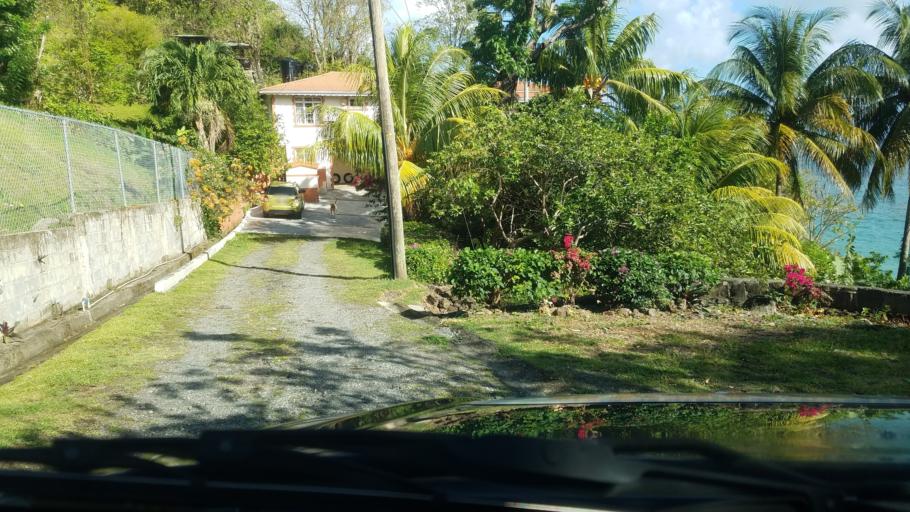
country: LC
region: Castries Quarter
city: Bisee
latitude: 14.0240
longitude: -61.0002
